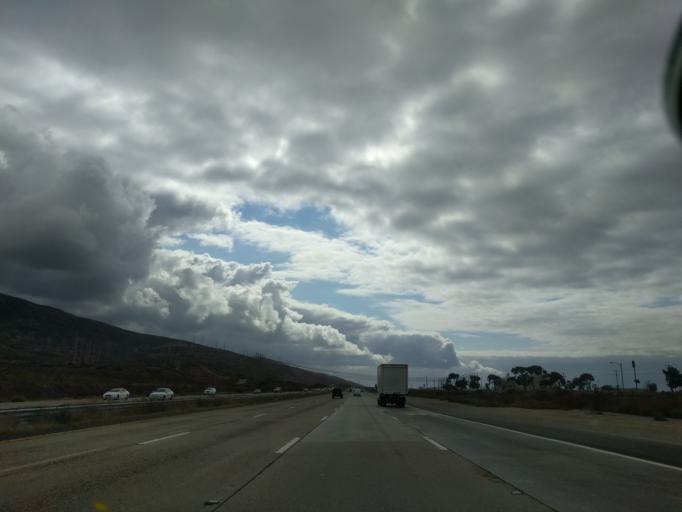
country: US
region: California
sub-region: Orange County
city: San Clemente
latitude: 33.3745
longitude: -117.5605
